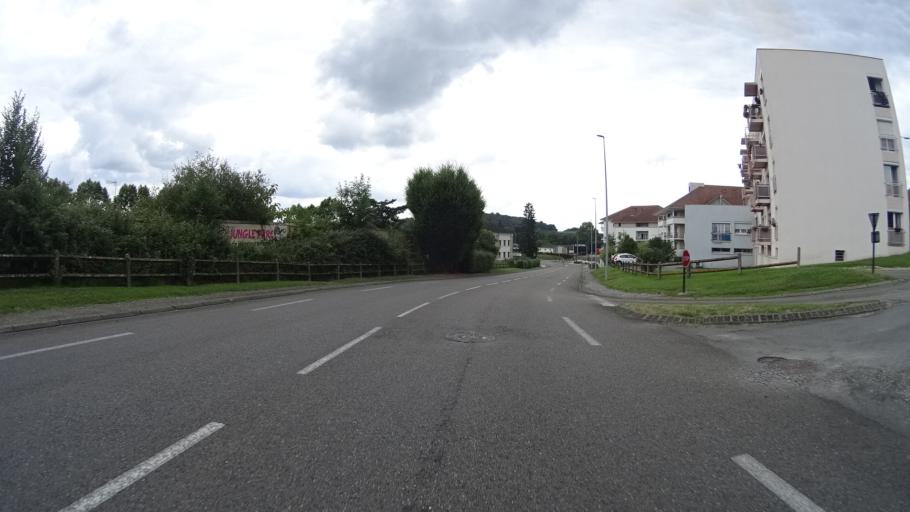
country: FR
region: Aquitaine
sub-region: Departement des Pyrenees-Atlantiques
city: Orthez
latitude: 43.4914
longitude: -0.7814
